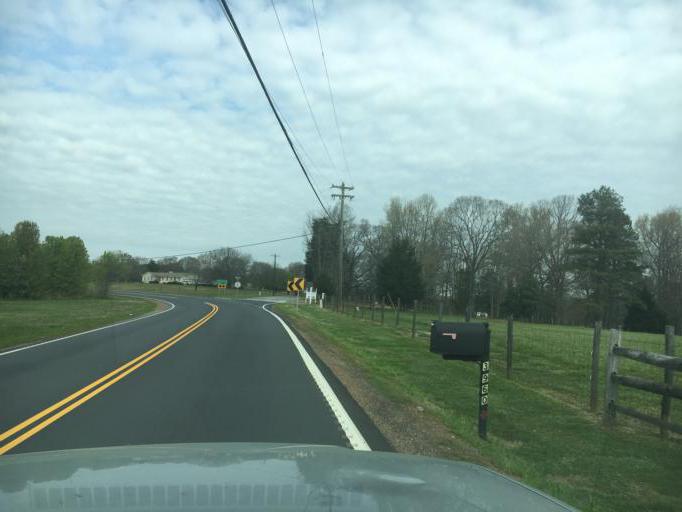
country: US
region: South Carolina
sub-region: Spartanburg County
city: Inman
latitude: 35.0231
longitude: -82.0845
